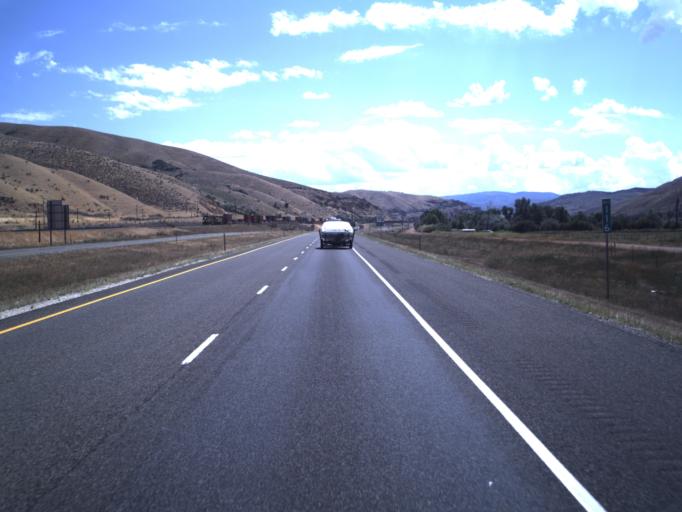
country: US
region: Utah
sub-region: Summit County
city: Coalville
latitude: 41.0101
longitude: -111.4821
